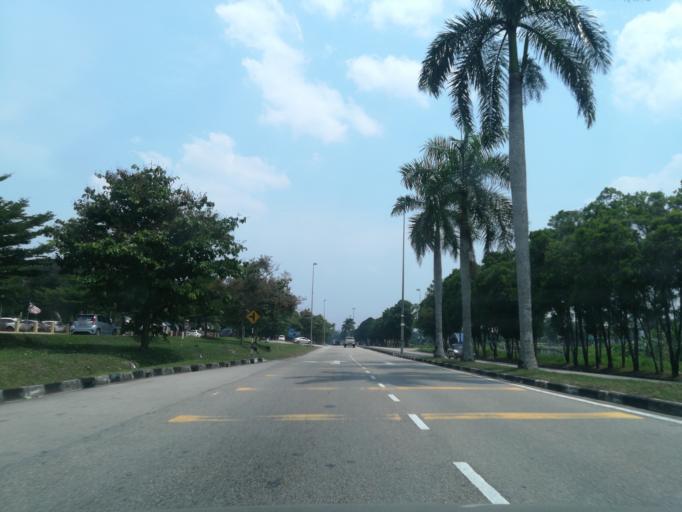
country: MY
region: Kedah
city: Kulim
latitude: 5.3927
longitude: 100.5725
